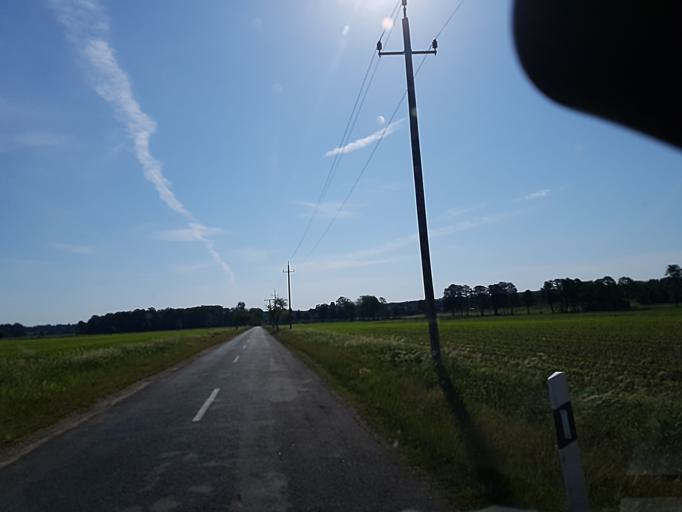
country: DE
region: Saxony-Anhalt
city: Rosslau
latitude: 52.0354
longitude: 12.2748
